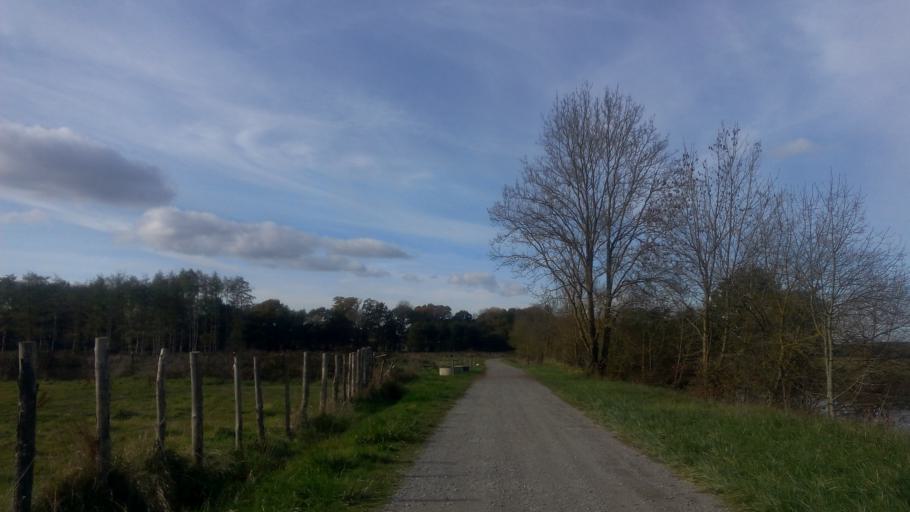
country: FR
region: Brittany
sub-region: Departement du Morbihan
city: Saint-Perreux
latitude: 47.6561
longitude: -2.1129
